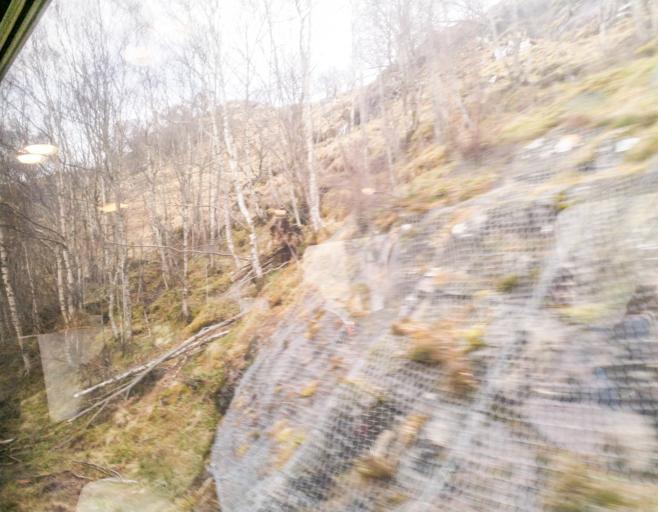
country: GB
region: Scotland
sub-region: Highland
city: Spean Bridge
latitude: 56.7949
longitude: -4.7243
